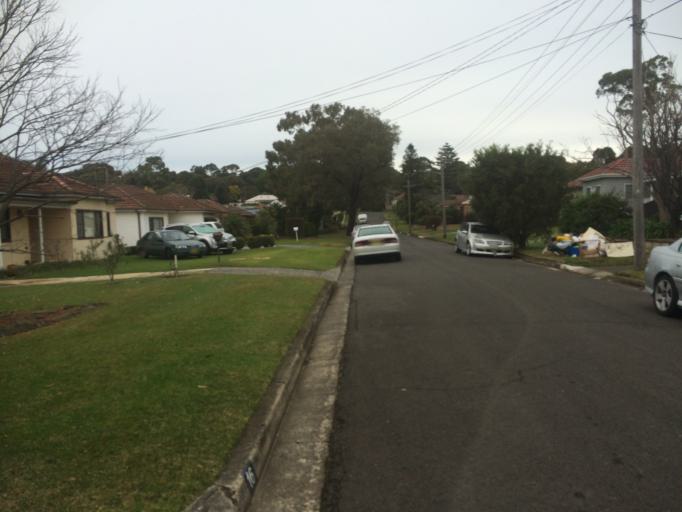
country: AU
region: New South Wales
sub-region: Sutherland Shire
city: Kirrawee
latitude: -34.0290
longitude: 151.0685
